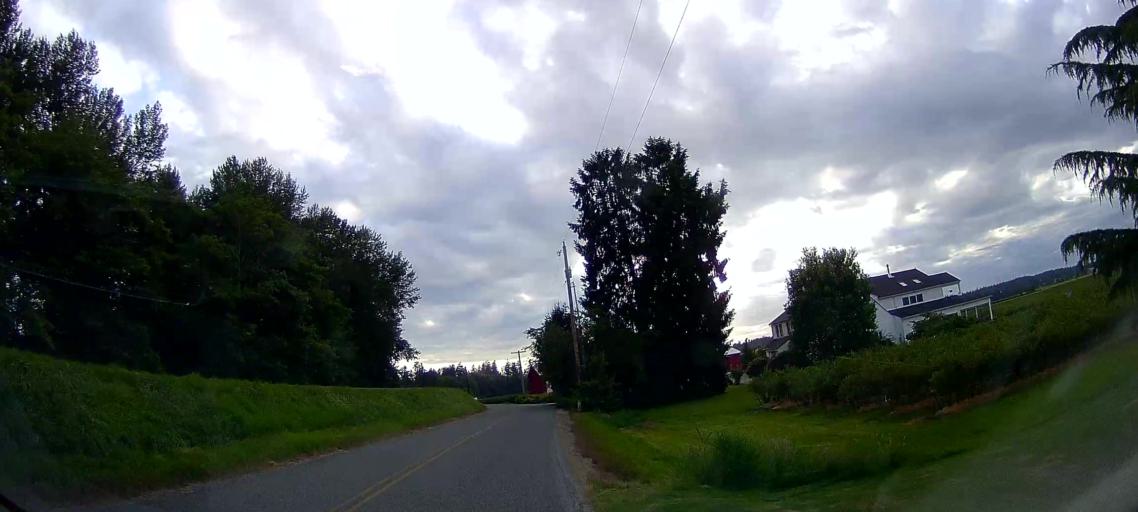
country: US
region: Washington
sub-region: Skagit County
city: Mount Vernon
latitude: 48.3673
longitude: -122.4115
